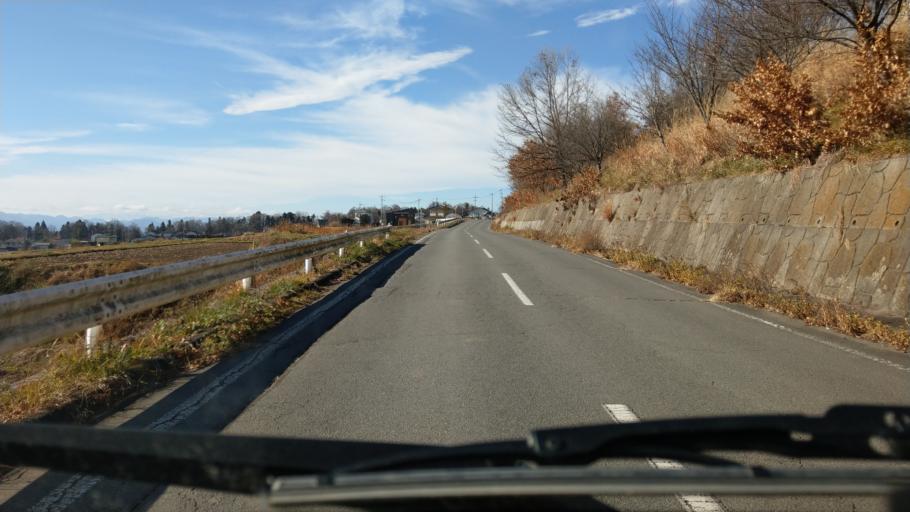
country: JP
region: Nagano
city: Komoro
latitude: 36.3294
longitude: 138.4525
